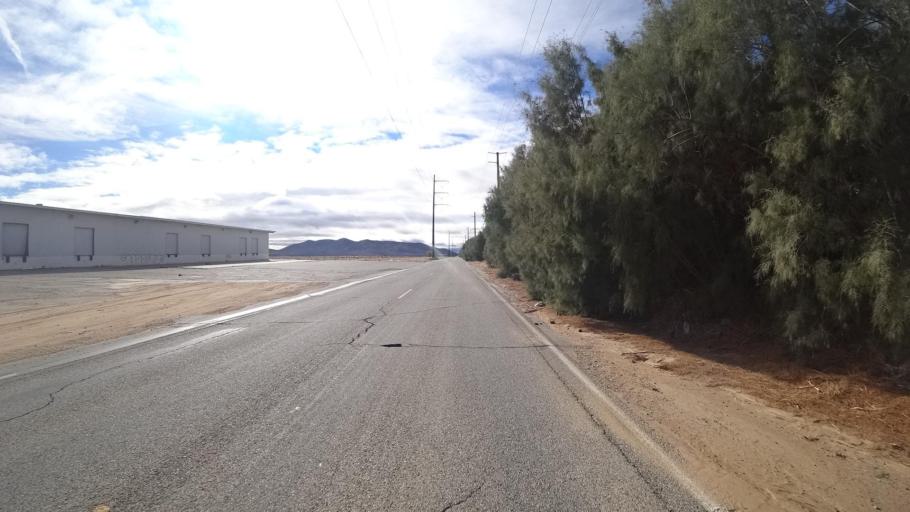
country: US
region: California
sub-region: Kern County
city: Rosamond
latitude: 34.9211
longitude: -118.2915
